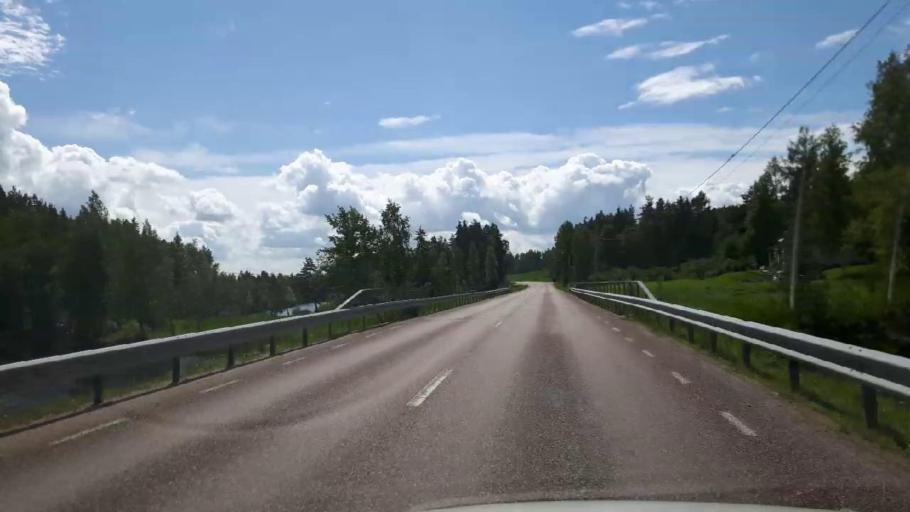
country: SE
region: Dalarna
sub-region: Faluns Kommun
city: Falun
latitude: 60.6318
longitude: 15.7681
